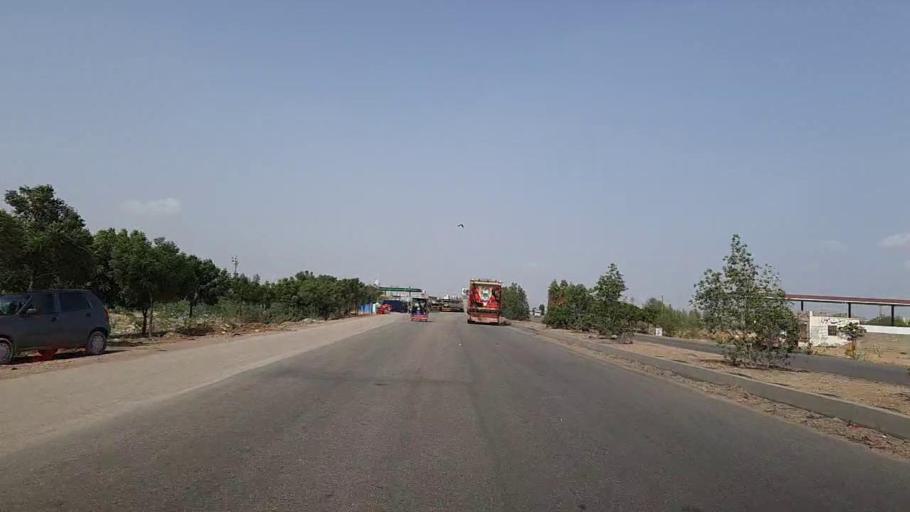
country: PK
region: Sindh
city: Malir Cantonment
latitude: 24.8679
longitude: 67.3720
